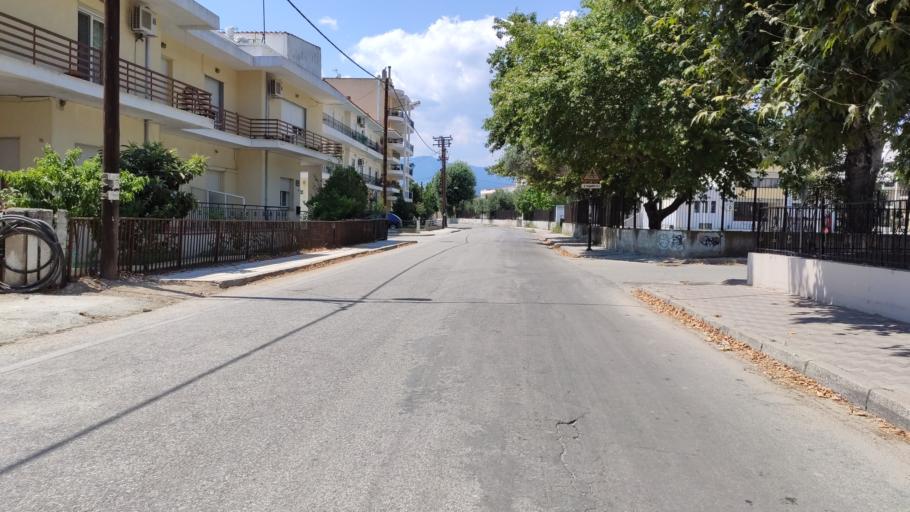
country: GR
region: East Macedonia and Thrace
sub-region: Nomos Rodopis
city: Komotini
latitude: 41.1202
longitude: 25.3950
